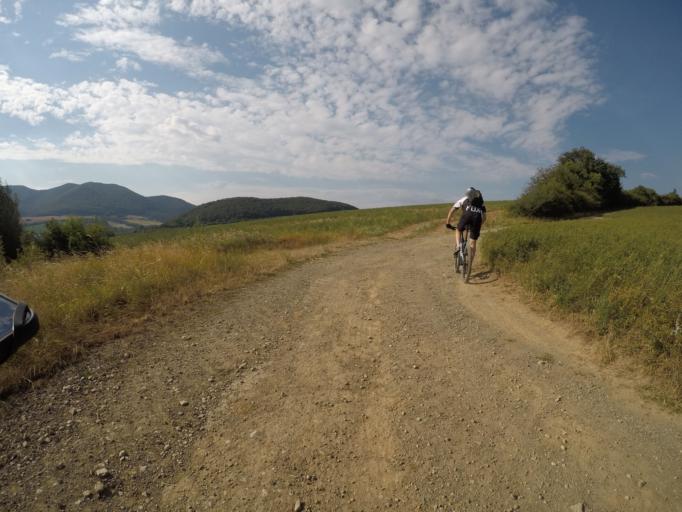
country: SK
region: Trenciansky
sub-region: Okres Trencin
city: Trencin
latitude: 48.8940
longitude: 17.9656
